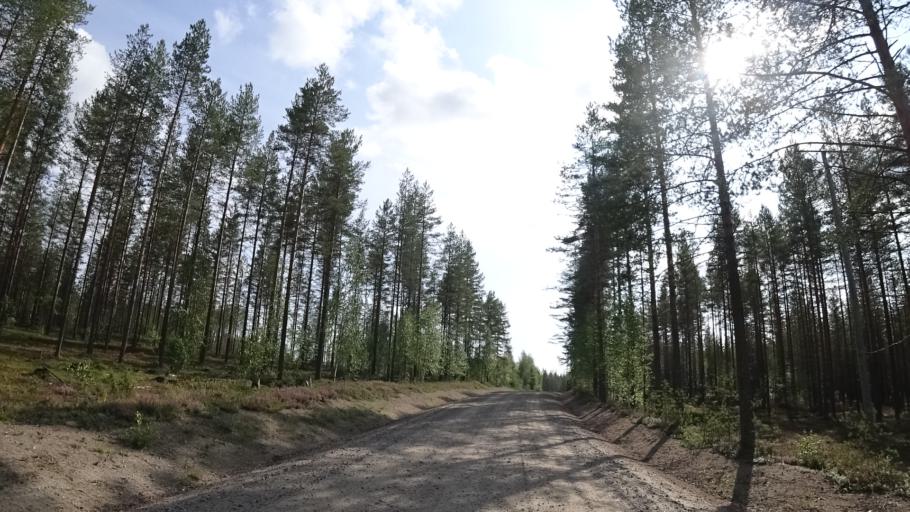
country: FI
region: North Karelia
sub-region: Pielisen Karjala
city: Lieksa
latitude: 63.5557
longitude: 30.0638
